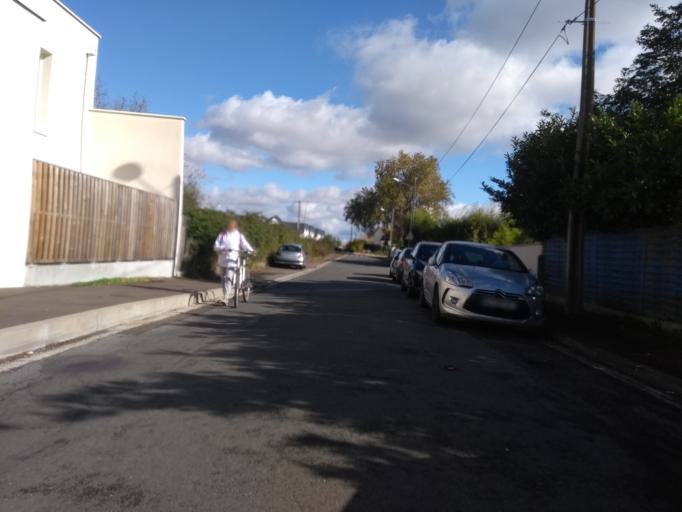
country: FR
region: Aquitaine
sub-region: Departement de la Gironde
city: Pessac
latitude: 44.8251
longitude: -0.6646
